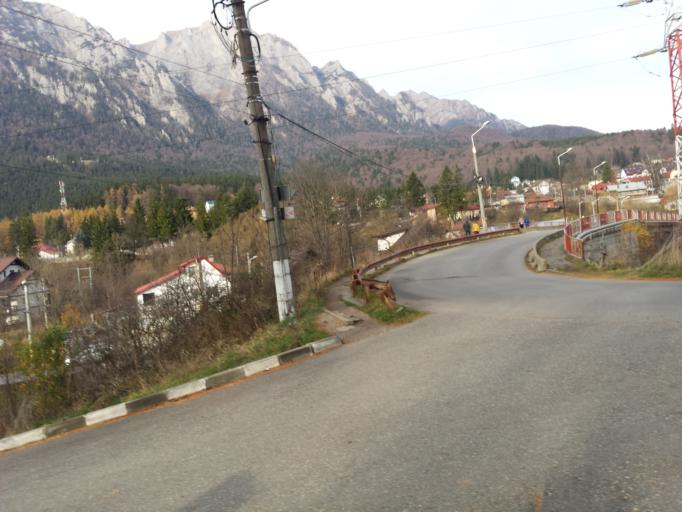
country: RO
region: Prahova
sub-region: Oras Busteni
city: Busteni
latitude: 45.4149
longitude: 25.5413
